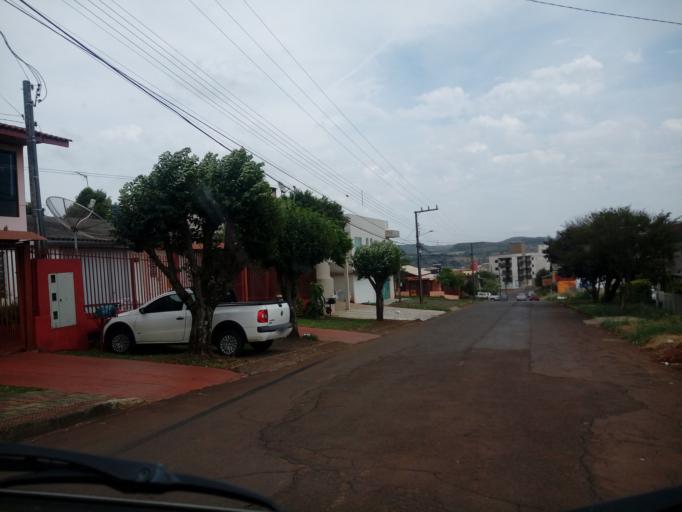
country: BR
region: Santa Catarina
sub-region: Chapeco
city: Chapeco
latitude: -27.0733
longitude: -52.6282
